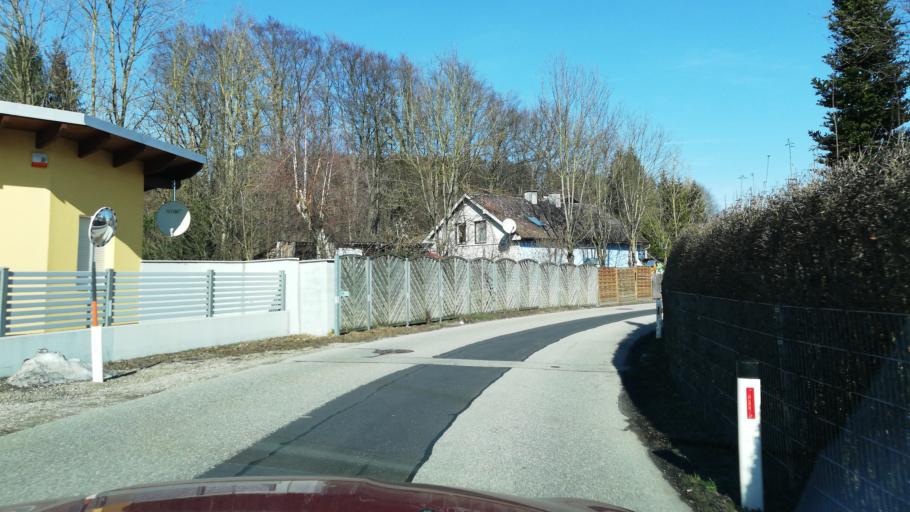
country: AT
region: Upper Austria
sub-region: Politischer Bezirk Vocklabruck
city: Attnang-Puchheim
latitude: 47.9936
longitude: 13.7035
